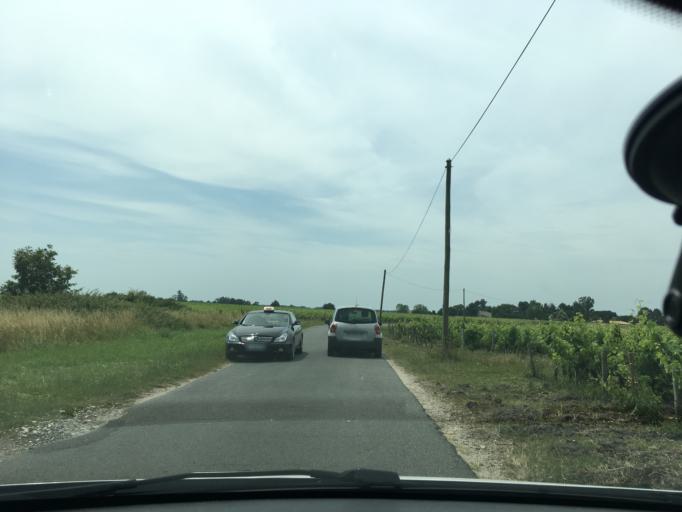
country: FR
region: Aquitaine
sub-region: Departement de la Gironde
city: Listrac-Medoc
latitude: 45.0673
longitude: -0.7968
